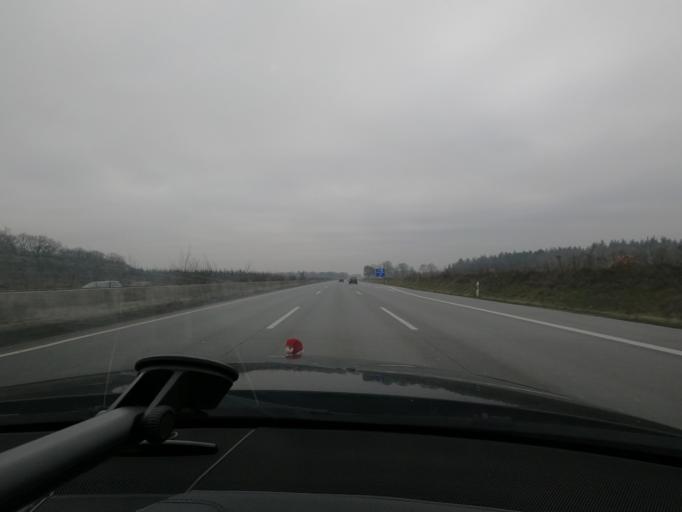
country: DE
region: Schleswig-Holstein
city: Bonningstedt
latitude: 53.6750
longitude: 9.9423
